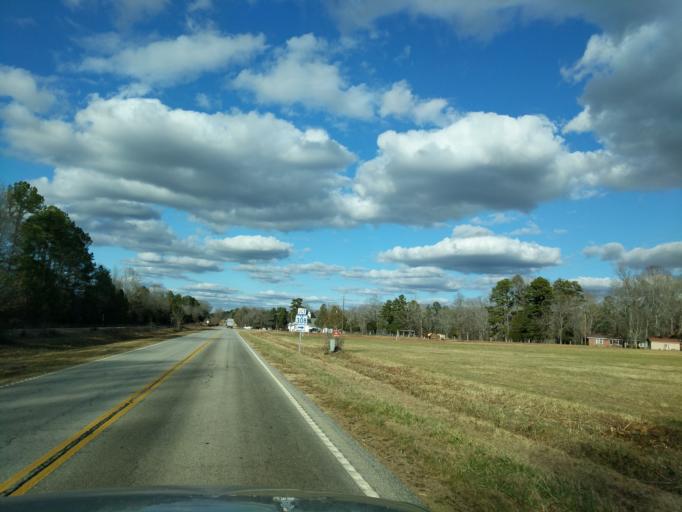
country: US
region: South Carolina
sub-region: Laurens County
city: Watts Mills
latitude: 34.5773
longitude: -81.9974
